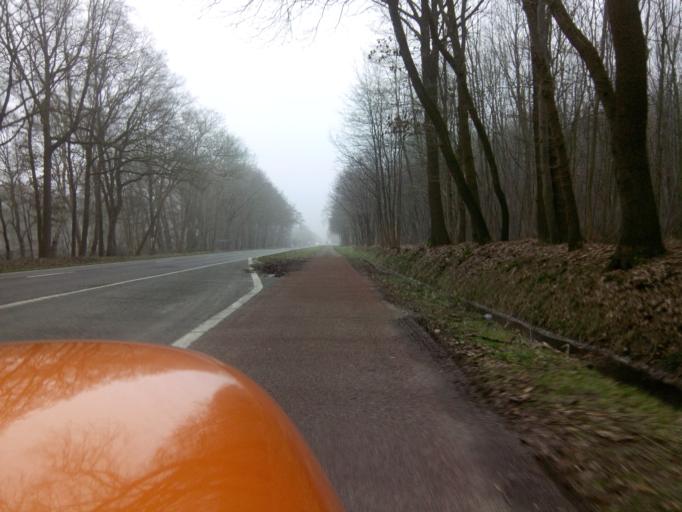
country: NL
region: Gelderland
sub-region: Gemeente Barneveld
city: Voorthuizen
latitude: 52.1916
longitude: 5.6307
